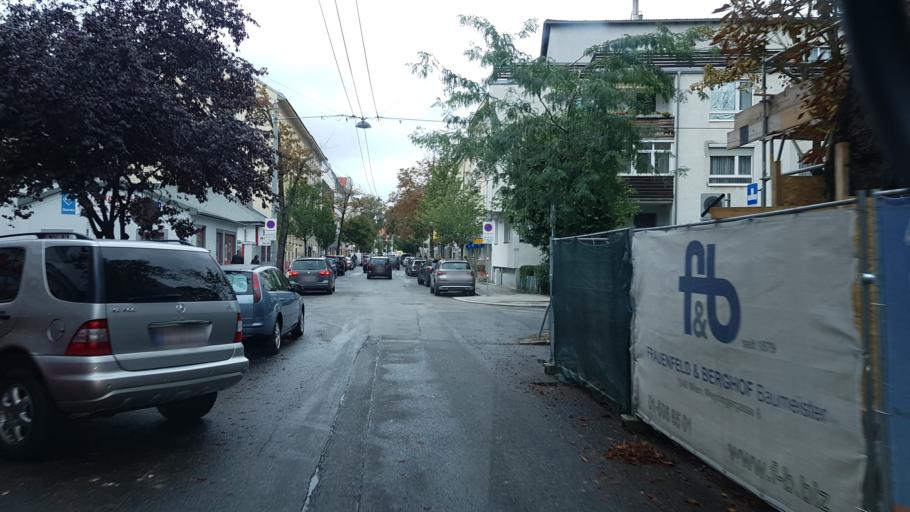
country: AT
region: Vienna
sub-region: Wien Stadt
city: Vienna
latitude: 48.2435
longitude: 16.3419
